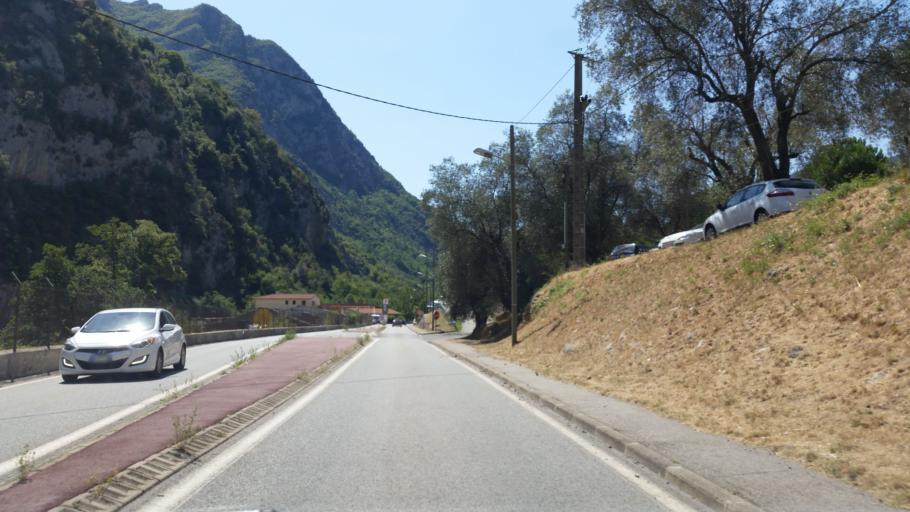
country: FR
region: Provence-Alpes-Cote d'Azur
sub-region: Departement des Alpes-Maritimes
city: Breil-sur-Roya
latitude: 43.9573
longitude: 7.5207
